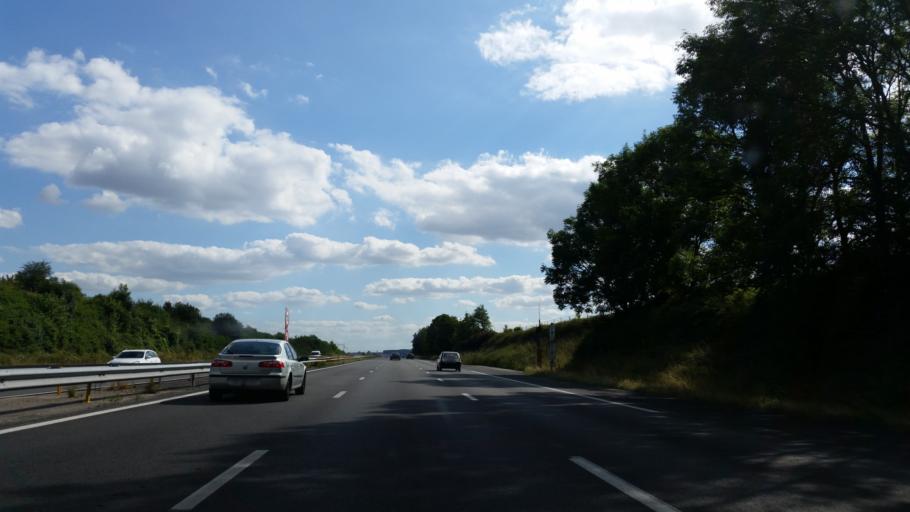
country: FR
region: Picardie
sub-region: Departement de la Somme
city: Peronne
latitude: 49.9869
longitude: 2.8709
